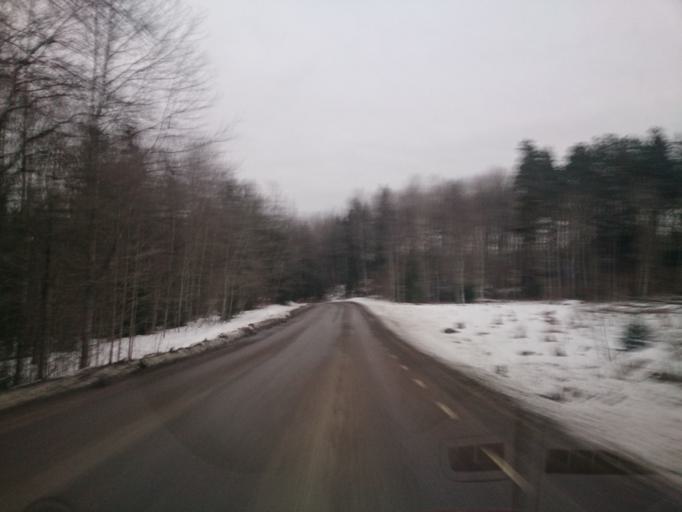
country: SE
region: OEstergoetland
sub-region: Atvidabergs Kommun
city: Atvidaberg
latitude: 58.2805
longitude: 16.0355
